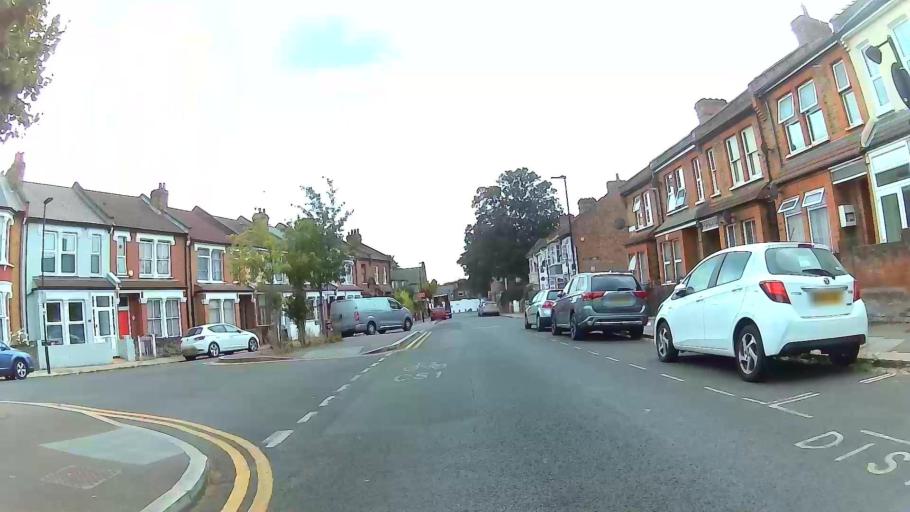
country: GB
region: England
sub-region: Greater London
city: Harringay
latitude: 51.5904
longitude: -0.0767
